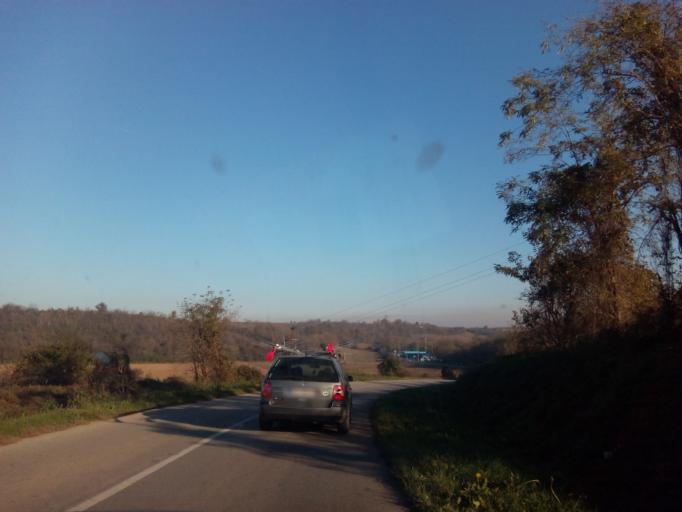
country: HR
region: Vukovarsko-Srijemska
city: Ilok
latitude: 45.2173
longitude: 19.4170
